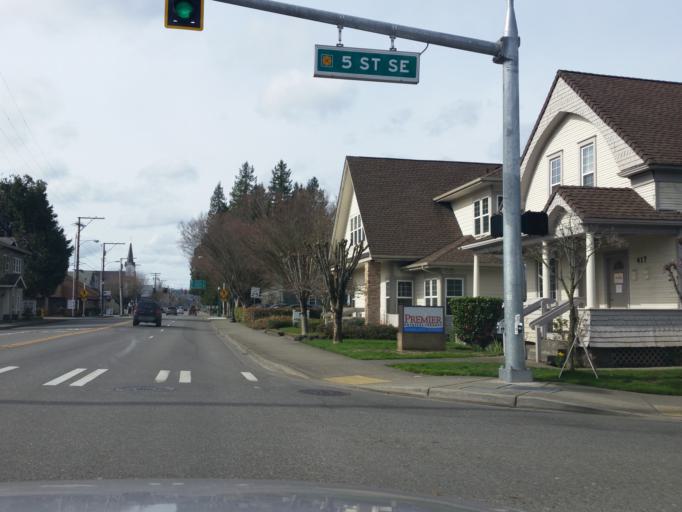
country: US
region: Washington
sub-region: Pierce County
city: Puyallup
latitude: 47.1905
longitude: -122.2884
